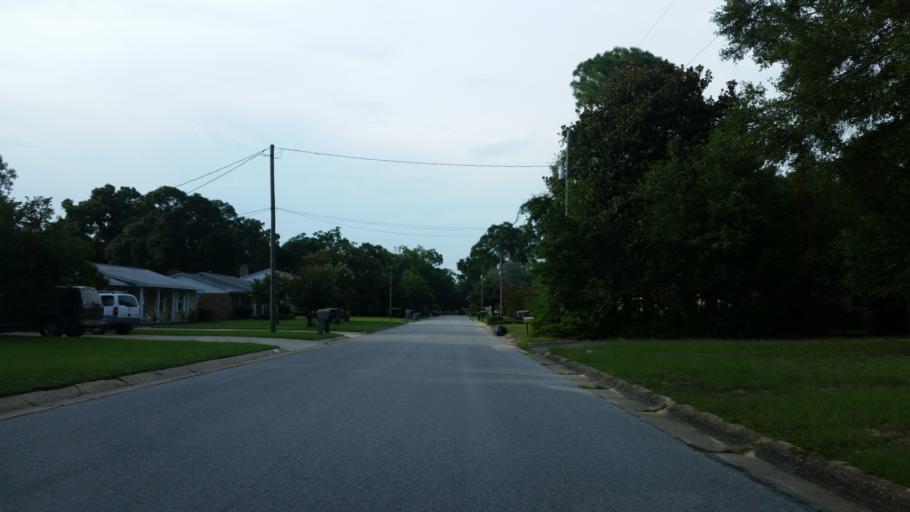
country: US
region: Florida
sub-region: Escambia County
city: Ferry Pass
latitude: 30.5105
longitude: -87.1895
